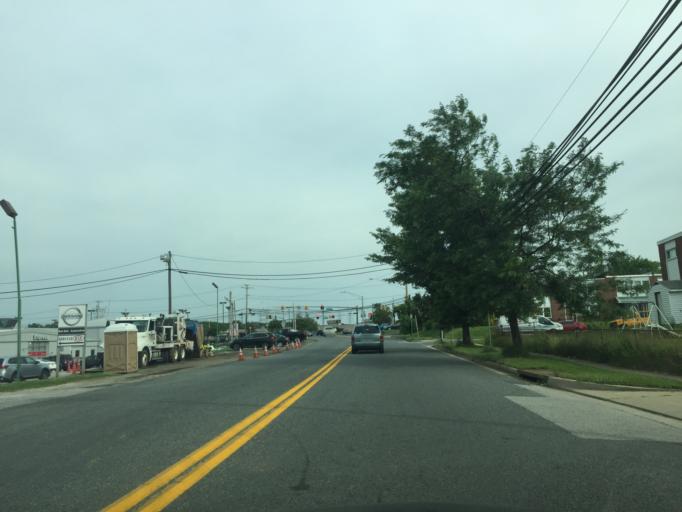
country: US
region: Maryland
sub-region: Baltimore County
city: Rosedale
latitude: 39.2969
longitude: -76.5104
